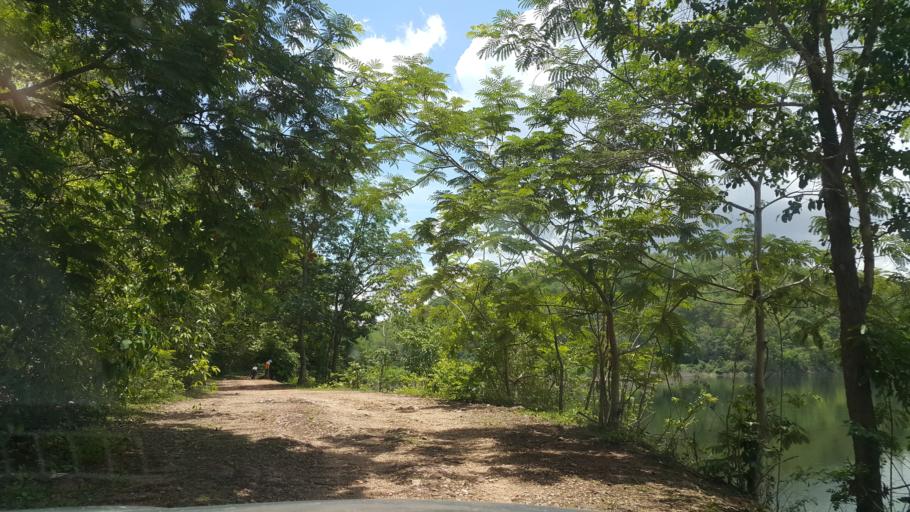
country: TH
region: Phayao
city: Phayao
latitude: 19.1860
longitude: 99.7984
